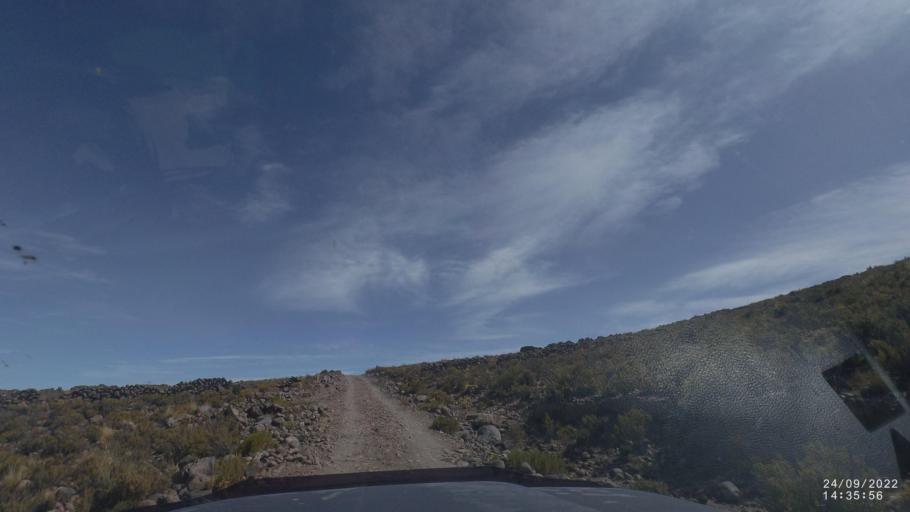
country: BO
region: Potosi
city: Colchani
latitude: -19.8530
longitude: -67.5786
